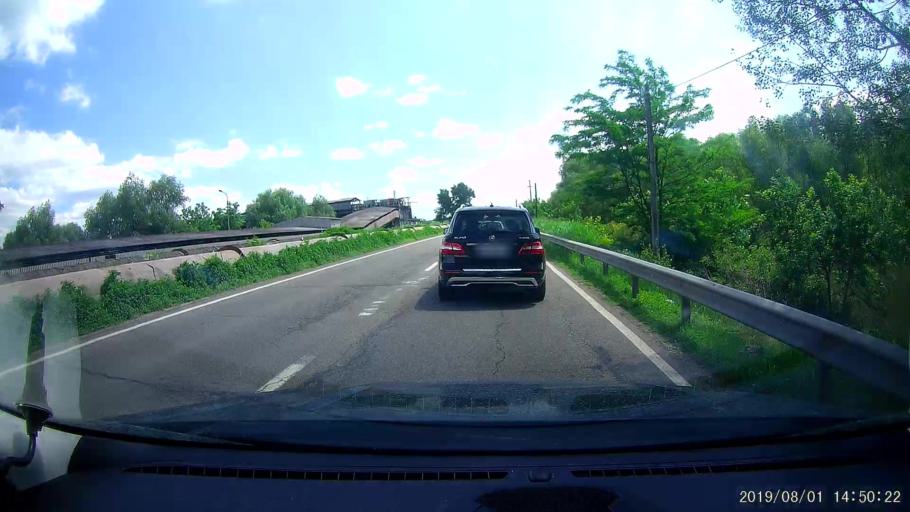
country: RO
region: Galati
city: Galati
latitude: 45.3905
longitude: 28.0158
